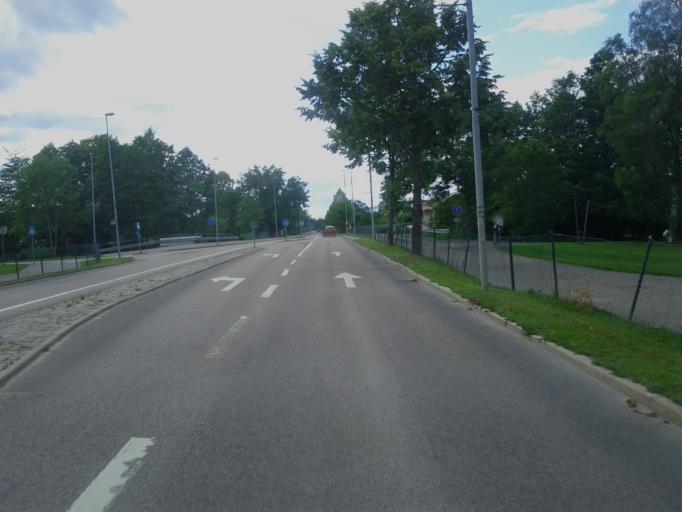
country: SE
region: Vaestmanland
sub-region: Sala Kommun
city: Sala
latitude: 59.9201
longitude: 16.5972
